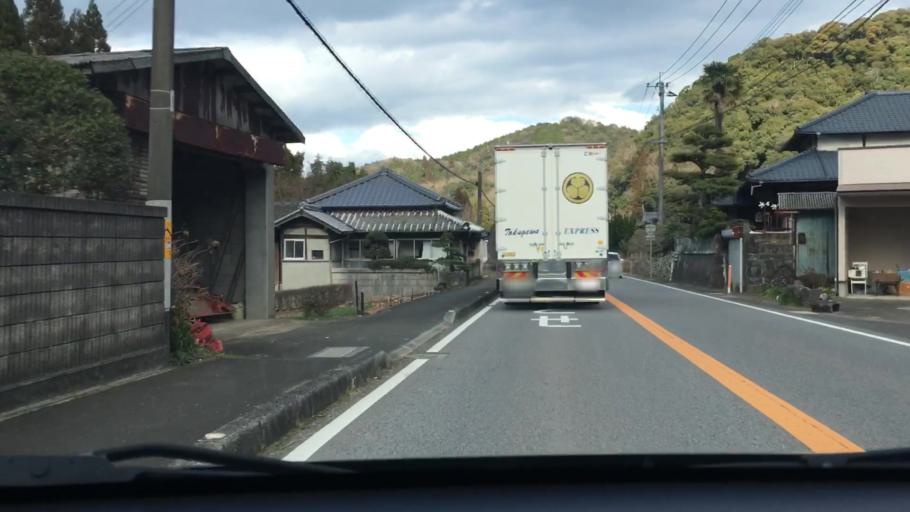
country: JP
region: Oita
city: Usuki
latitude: 33.0156
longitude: 131.7007
